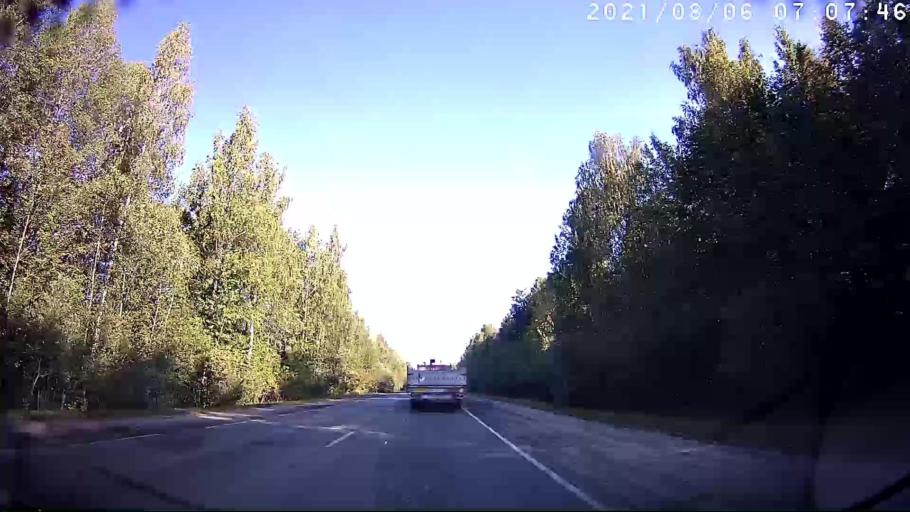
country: RU
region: Mariy-El
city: Yoshkar-Ola
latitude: 56.5653
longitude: 47.9766
